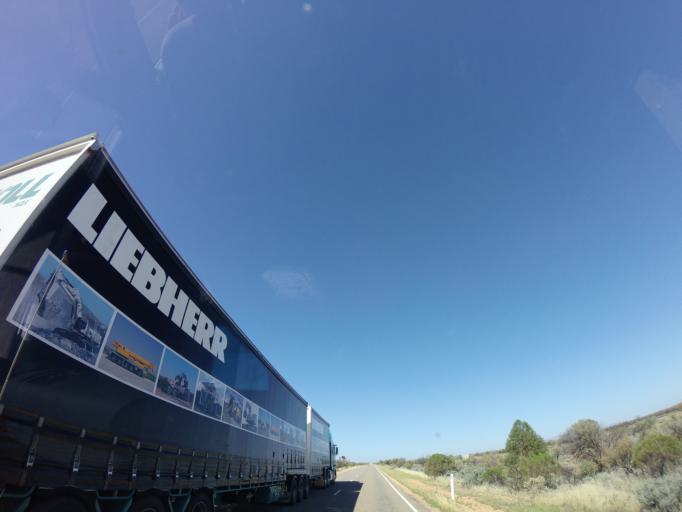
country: AU
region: South Australia
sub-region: Peterborough
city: Peterborough
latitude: -32.5760
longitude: 139.5770
